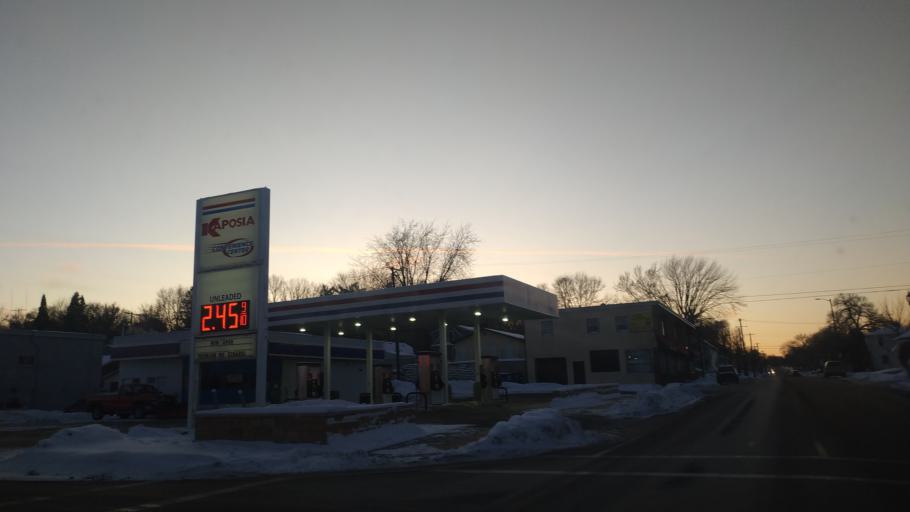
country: US
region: Minnesota
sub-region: Dakota County
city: South Saint Paul
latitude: 44.8890
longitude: -93.0500
